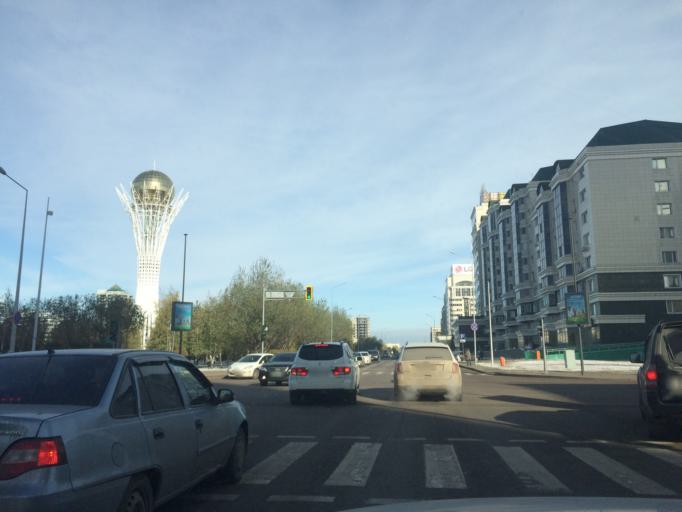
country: KZ
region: Astana Qalasy
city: Astana
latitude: 51.1254
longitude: 71.4314
